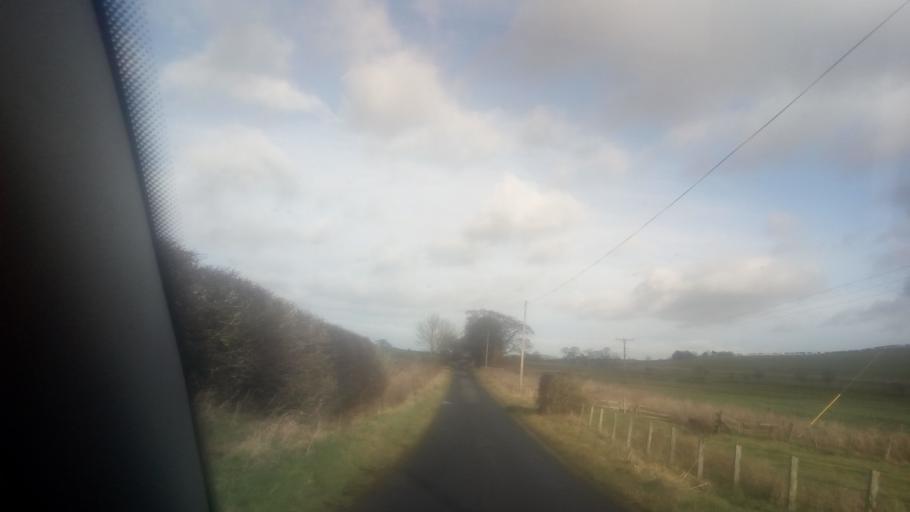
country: GB
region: Scotland
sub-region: The Scottish Borders
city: Kelso
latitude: 55.4967
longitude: -2.4280
